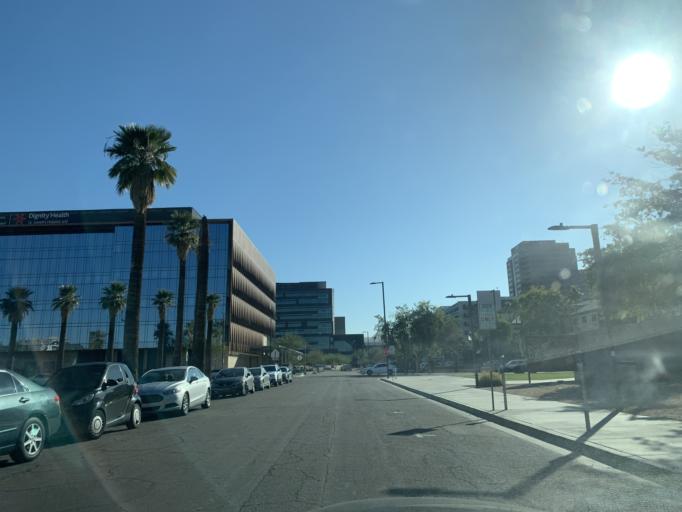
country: US
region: Arizona
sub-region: Maricopa County
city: Phoenix
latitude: 33.4560
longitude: -112.0666
